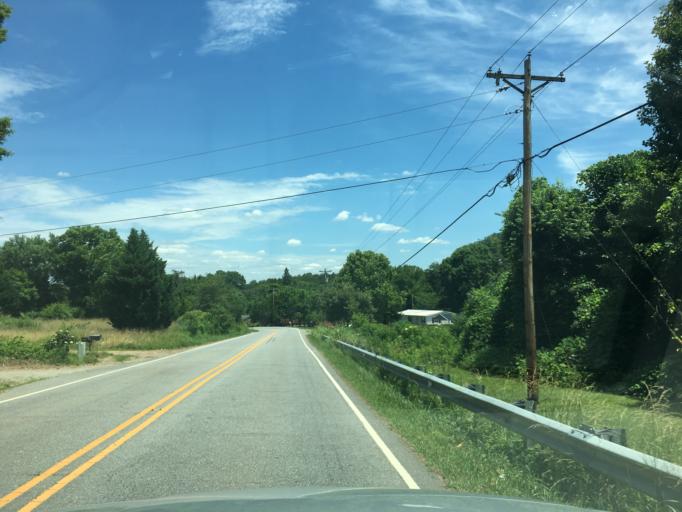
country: US
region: North Carolina
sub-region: Burke County
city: Glen Alpine
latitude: 35.6739
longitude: -81.7687
